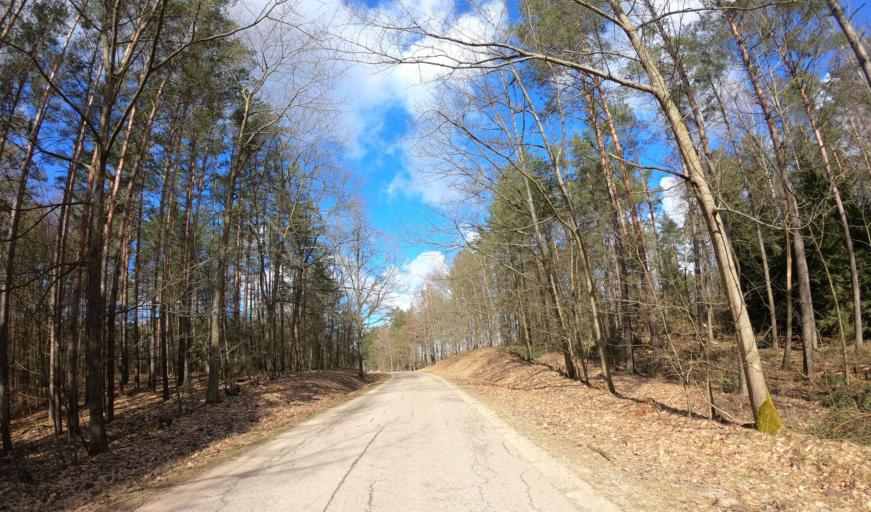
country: PL
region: West Pomeranian Voivodeship
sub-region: Powiat drawski
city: Zlocieniec
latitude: 53.4774
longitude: 15.9248
